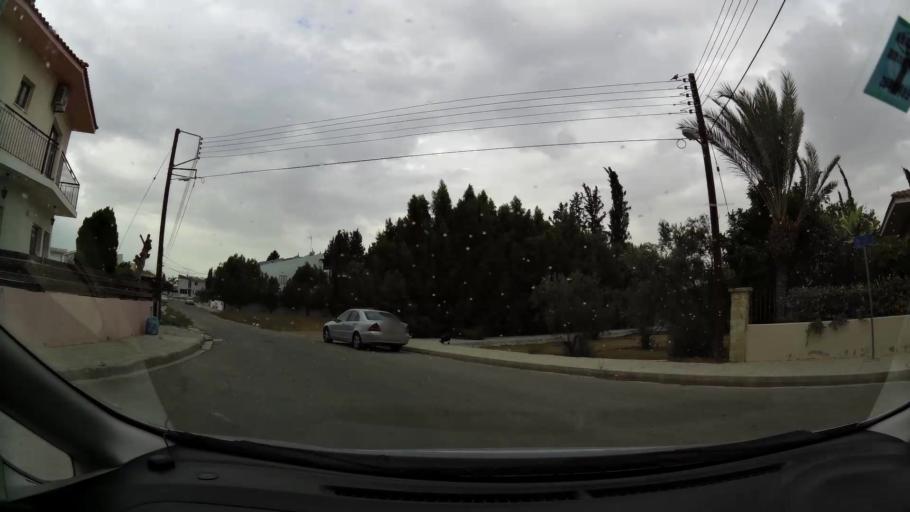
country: CY
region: Lefkosia
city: Geri
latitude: 35.1061
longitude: 33.3911
